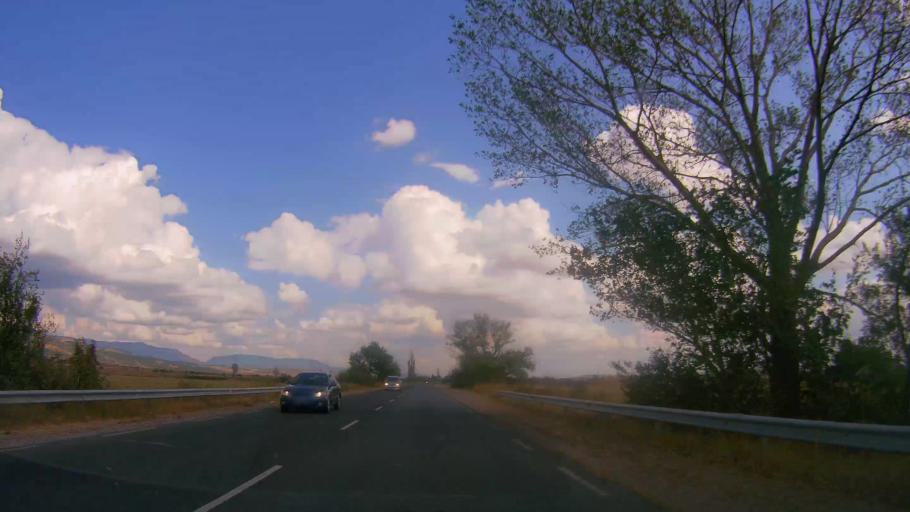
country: BG
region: Sliven
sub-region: Obshtina Sliven
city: Sliven
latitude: 42.6360
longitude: 26.2230
